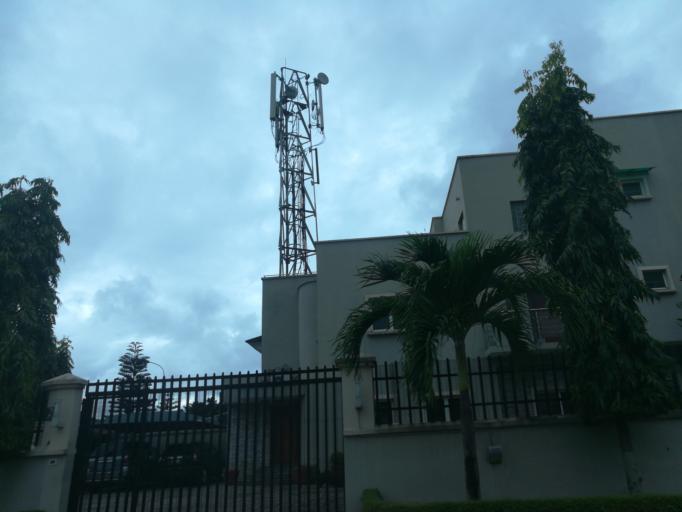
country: NG
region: Lagos
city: Ikoyi
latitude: 6.4467
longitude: 3.4571
